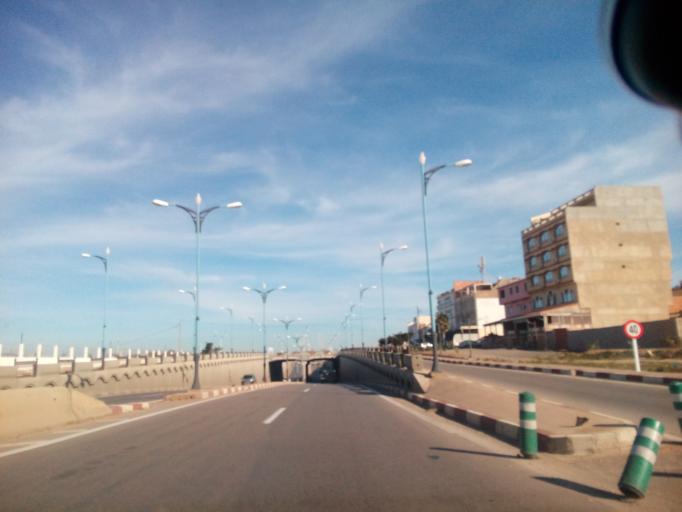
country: DZ
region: Mostaganem
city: Mostaganem
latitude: 35.8675
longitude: 0.0369
